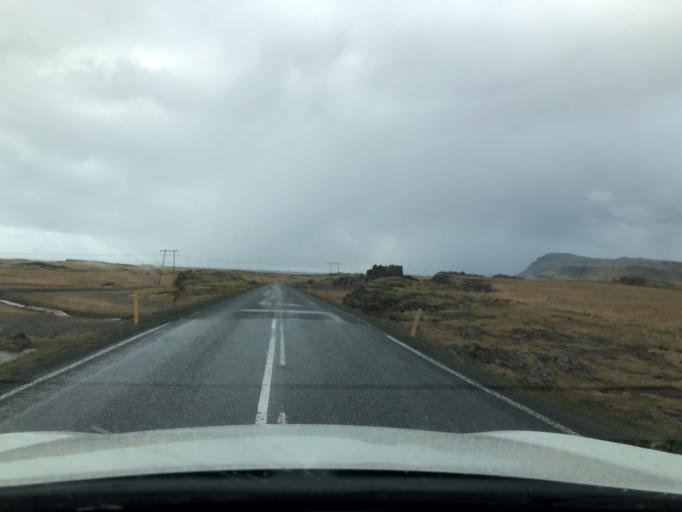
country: IS
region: East
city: Hoefn
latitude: 64.2433
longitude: -15.6785
